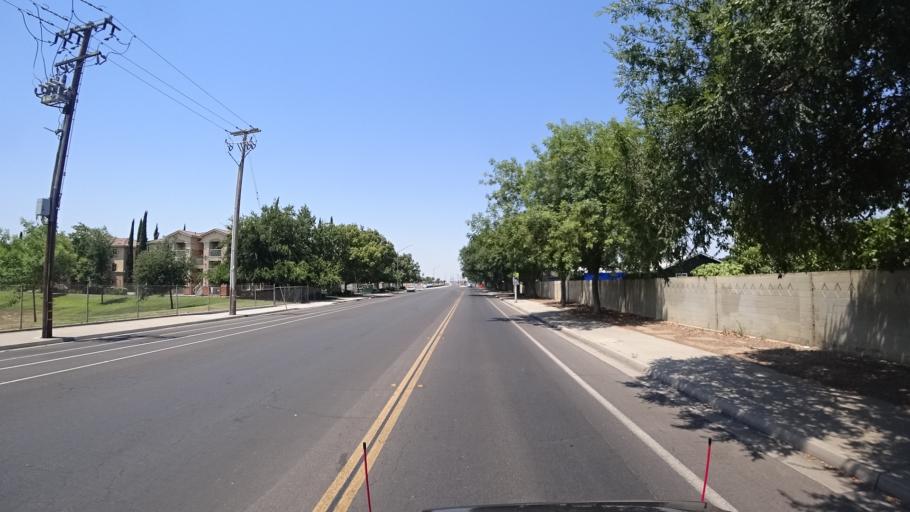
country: US
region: California
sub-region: Fresno County
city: Fresno
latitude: 36.7142
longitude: -119.7958
